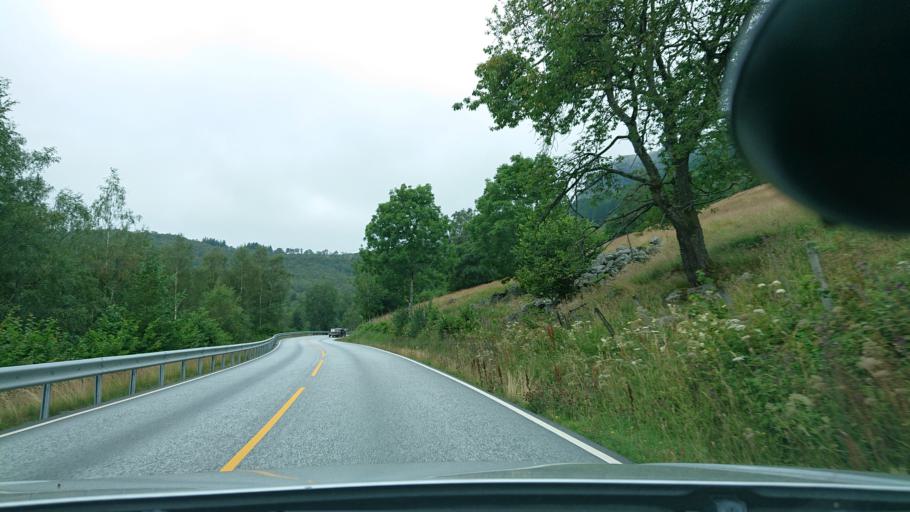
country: NO
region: Rogaland
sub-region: Hjelmeland
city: Hjelmelandsvagen
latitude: 59.1701
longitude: 6.1680
